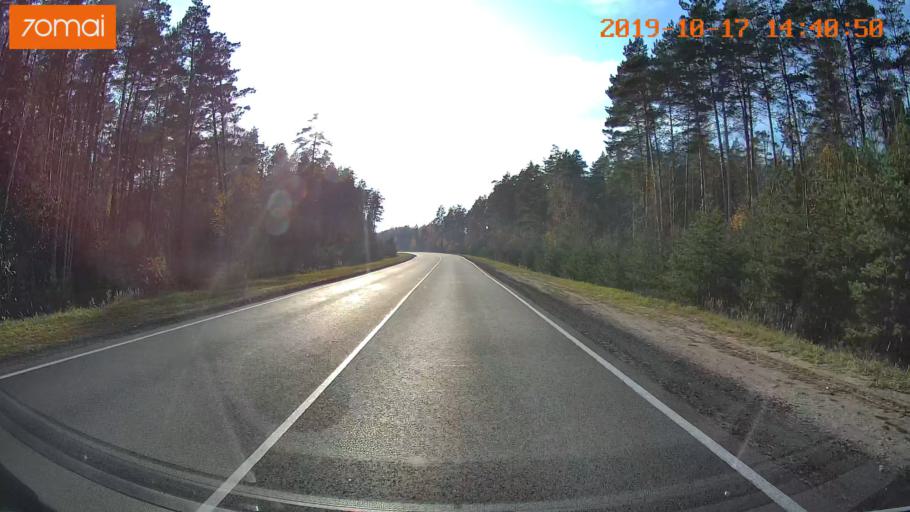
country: RU
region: Rjazan
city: Solotcha
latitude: 54.8522
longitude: 39.9486
